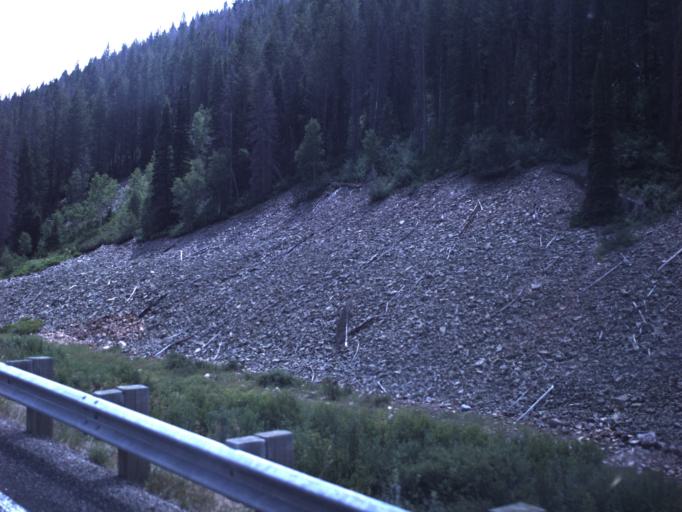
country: US
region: Utah
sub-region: Summit County
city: Francis
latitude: 40.5177
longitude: -111.0799
